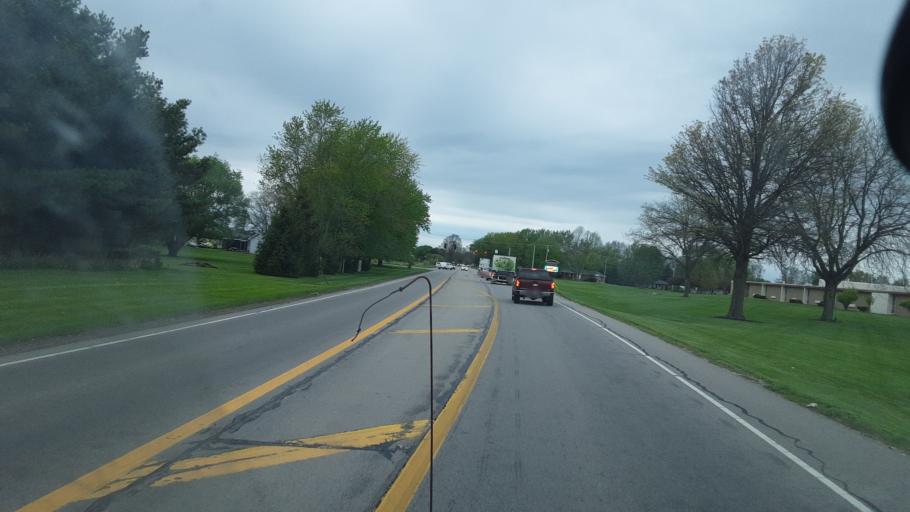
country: US
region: Indiana
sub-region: Elkhart County
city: New Paris
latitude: 41.5163
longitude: -85.7681
